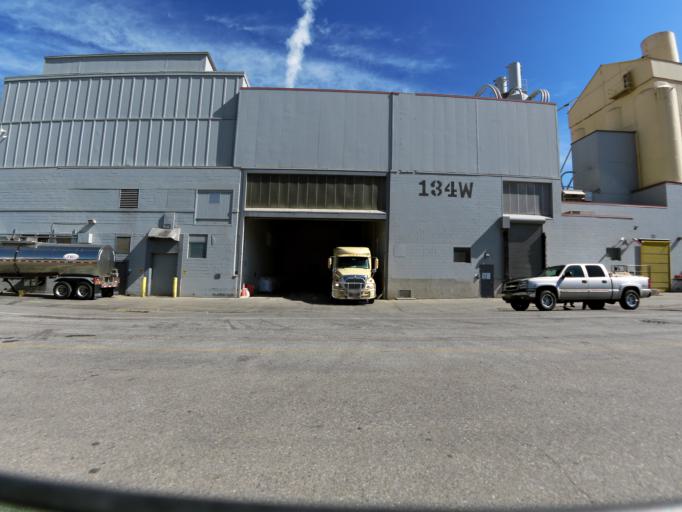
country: US
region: Utah
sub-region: Weber County
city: Ogden
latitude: 41.2125
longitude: -111.9807
